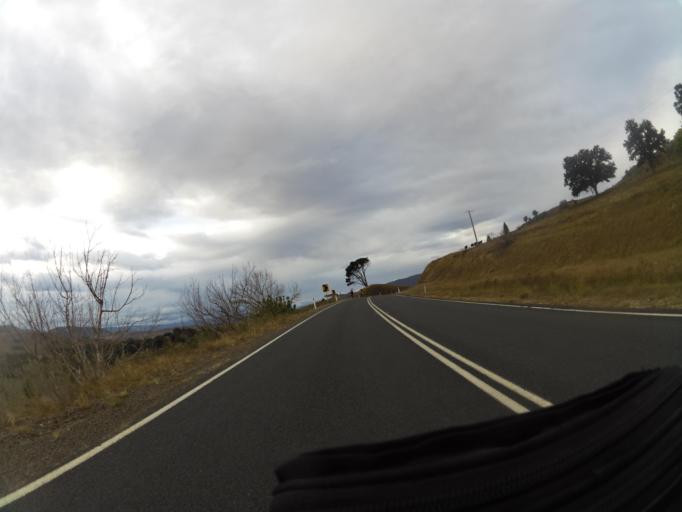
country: AU
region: New South Wales
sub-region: Snowy River
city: Jindabyne
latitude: -36.0847
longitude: 147.9780
